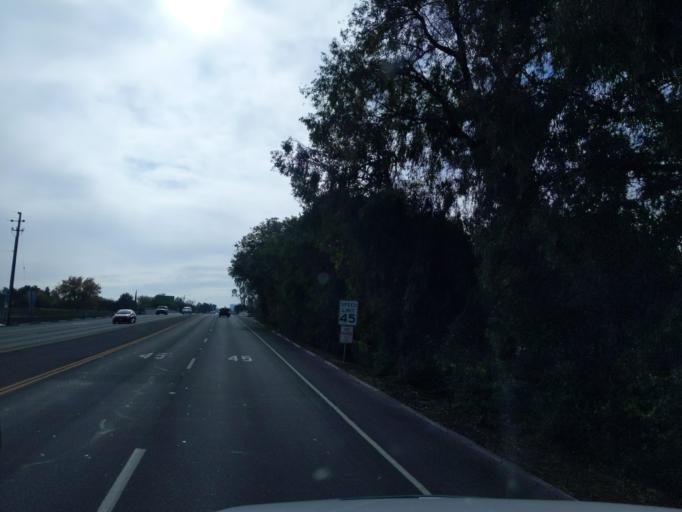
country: US
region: California
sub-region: San Joaquin County
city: August
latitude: 37.9910
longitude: -121.2671
